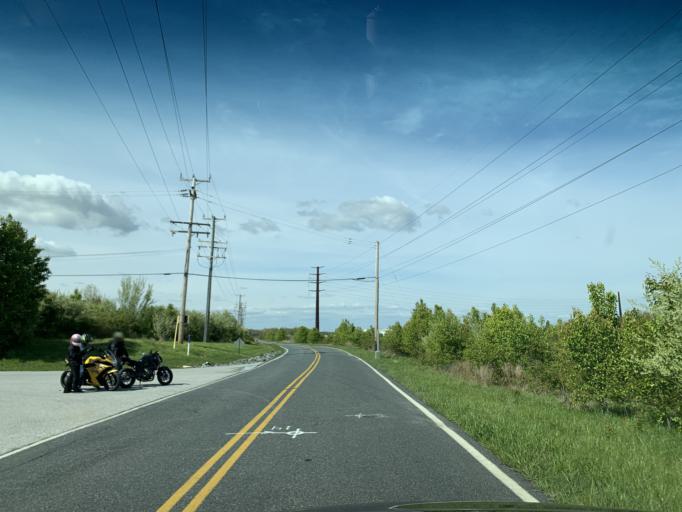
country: US
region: Maryland
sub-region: Harford County
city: Perryman
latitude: 39.4428
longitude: -76.2152
